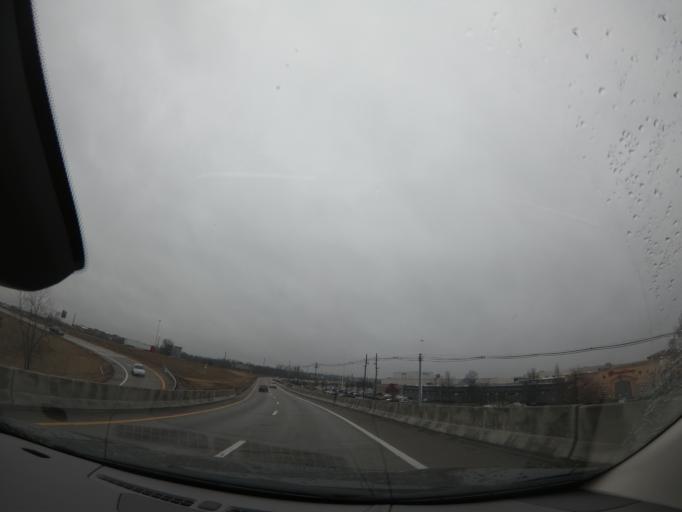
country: US
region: Kentucky
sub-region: Jefferson County
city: Beechwood Village
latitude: 38.2495
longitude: -85.6213
